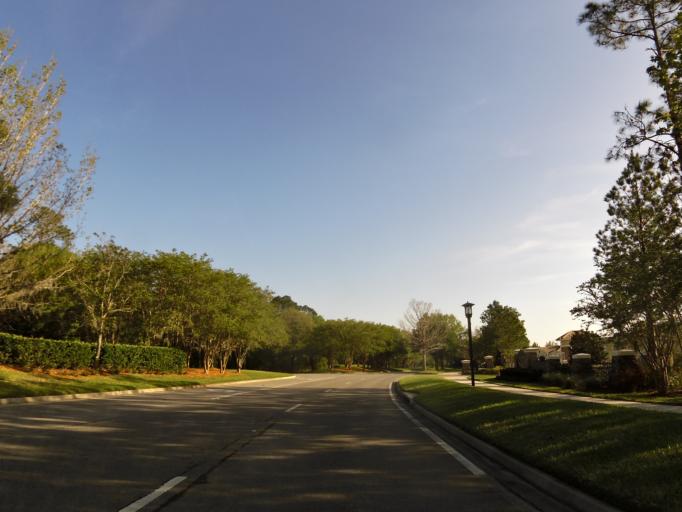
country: US
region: Florida
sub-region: Saint Johns County
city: Villano Beach
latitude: 29.9839
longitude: -81.4763
